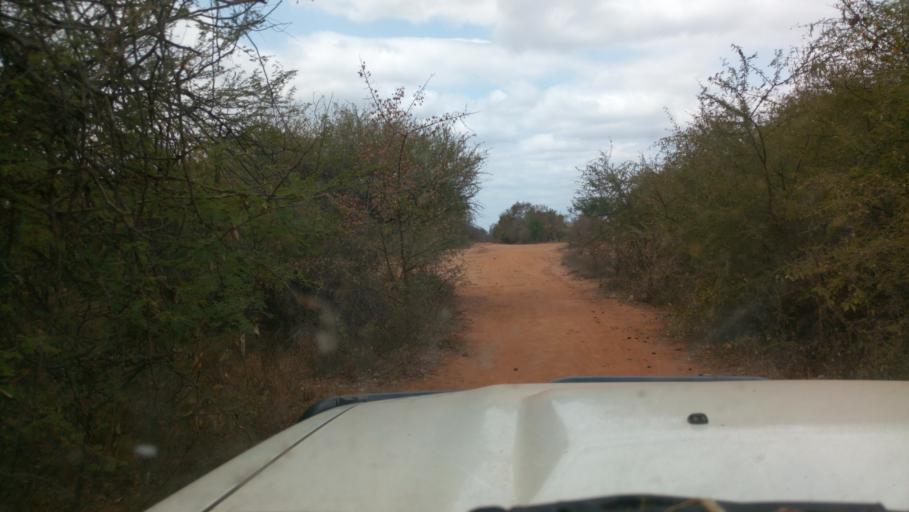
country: KE
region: Kitui
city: Kitui
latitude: -1.8679
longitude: 38.3675
